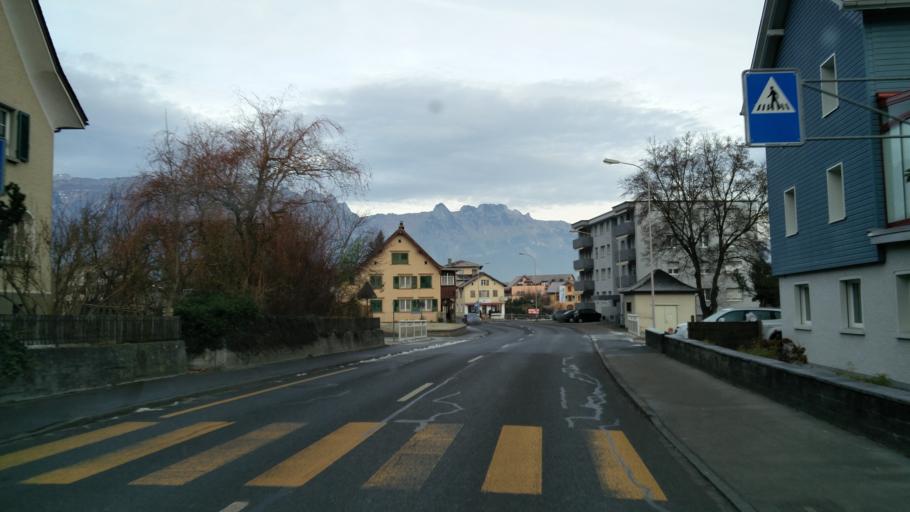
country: CH
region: Saint Gallen
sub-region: Wahlkreis Werdenberg
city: Buchs
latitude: 47.1607
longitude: 9.4759
